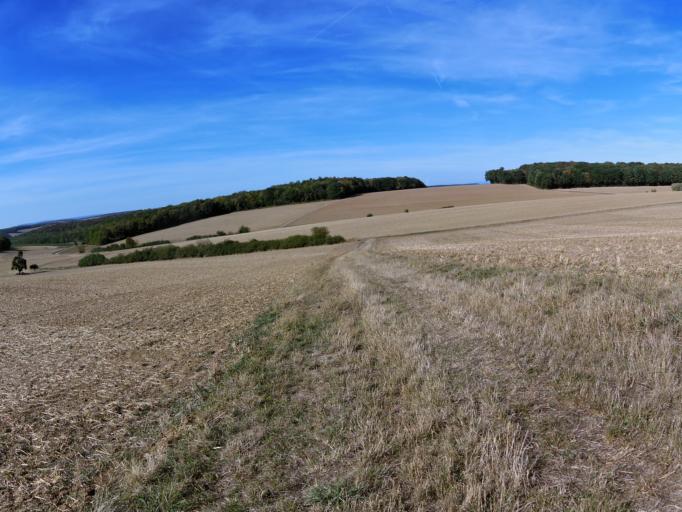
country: DE
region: Bavaria
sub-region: Regierungsbezirk Unterfranken
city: Eisingen
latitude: 49.7622
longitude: 9.8357
